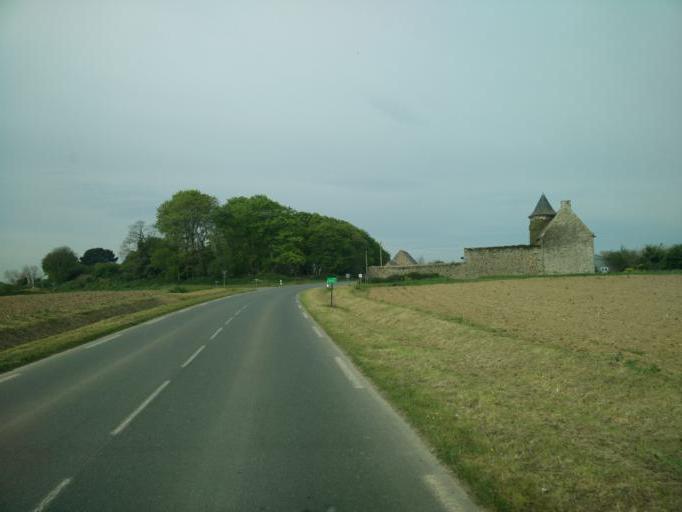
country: FR
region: Brittany
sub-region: Departement des Cotes-d'Armor
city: Pleubian
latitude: 48.8332
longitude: -3.1511
